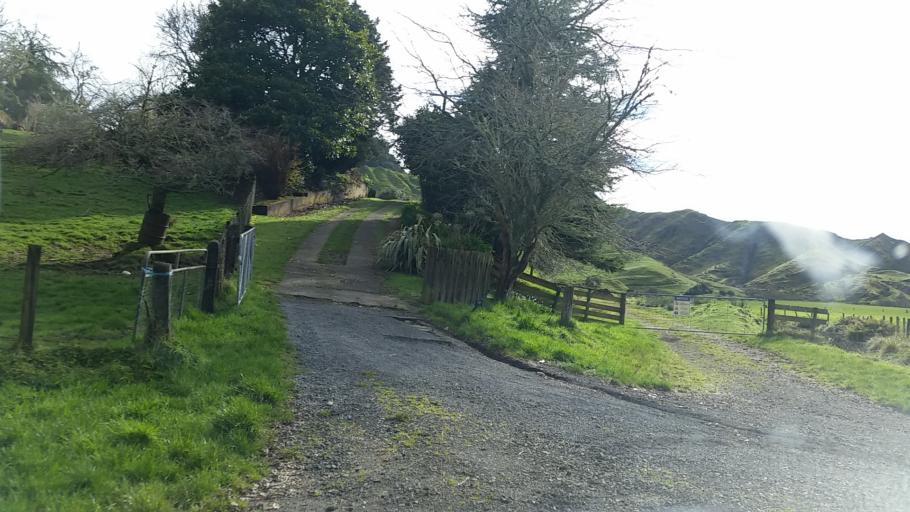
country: NZ
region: Taranaki
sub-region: South Taranaki District
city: Eltham
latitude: -39.2237
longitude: 174.5629
